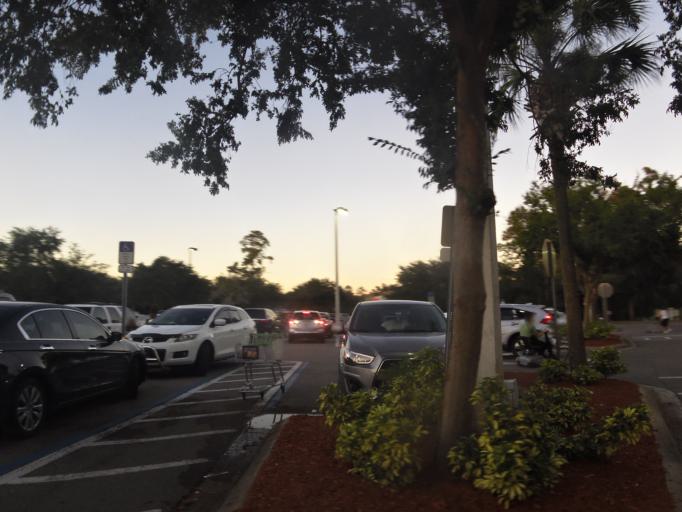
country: US
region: Florida
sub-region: Flagler County
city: Palm Coast
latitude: 29.5517
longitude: -81.2360
